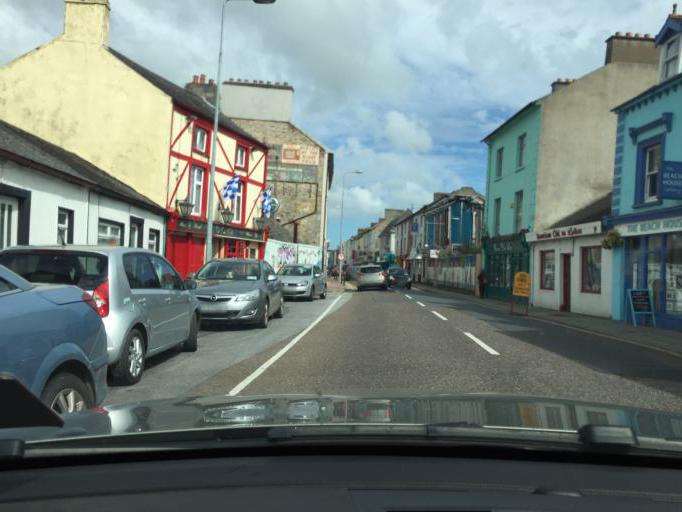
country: IE
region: Munster
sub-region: Waterford
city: Dungarvan
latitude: 52.0896
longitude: -7.6239
